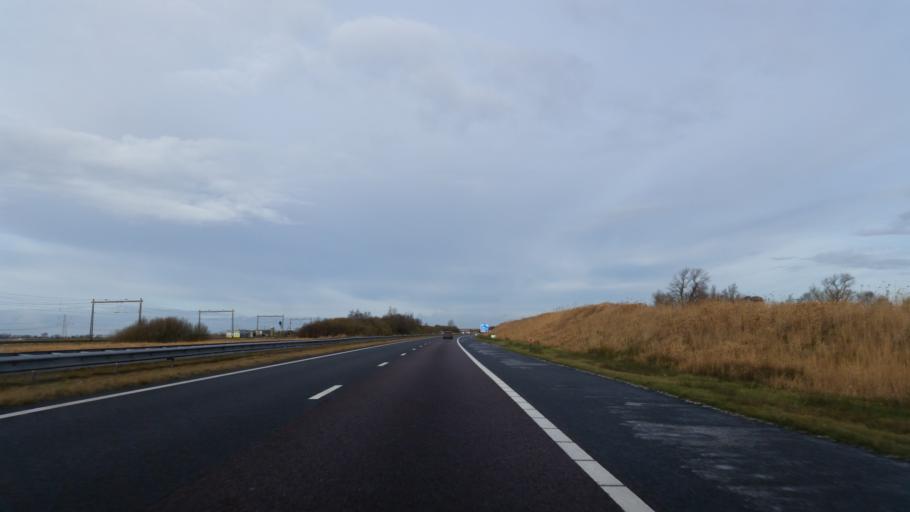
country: NL
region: Friesland
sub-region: Gemeente Boarnsterhim
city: Grou
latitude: 53.1022
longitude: 5.8172
